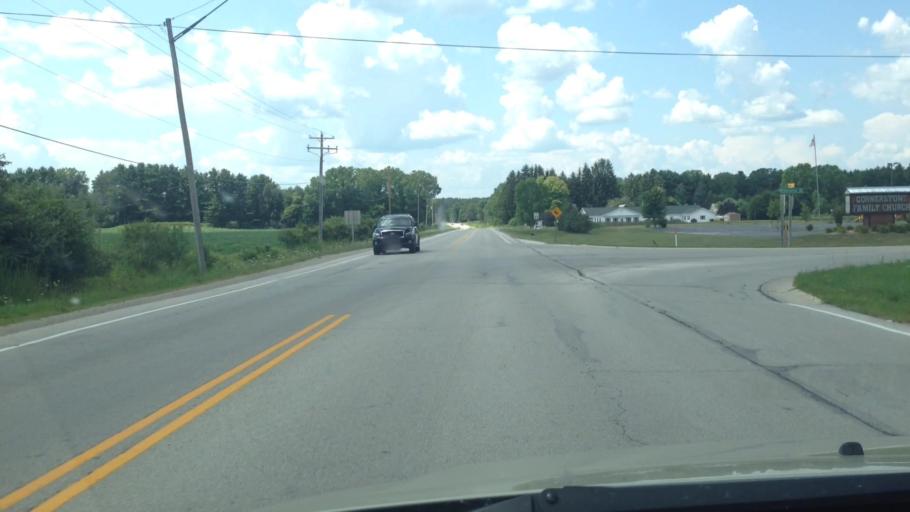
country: US
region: Wisconsin
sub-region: Brown County
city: Suamico
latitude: 44.6441
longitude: -88.0898
